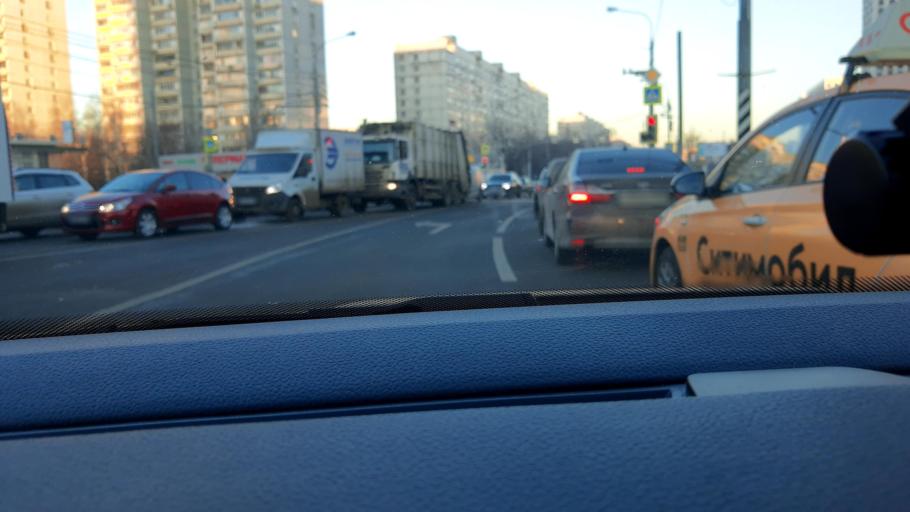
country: RU
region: Moscow
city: Orekhovo-Borisovo
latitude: 55.6003
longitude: 37.7270
